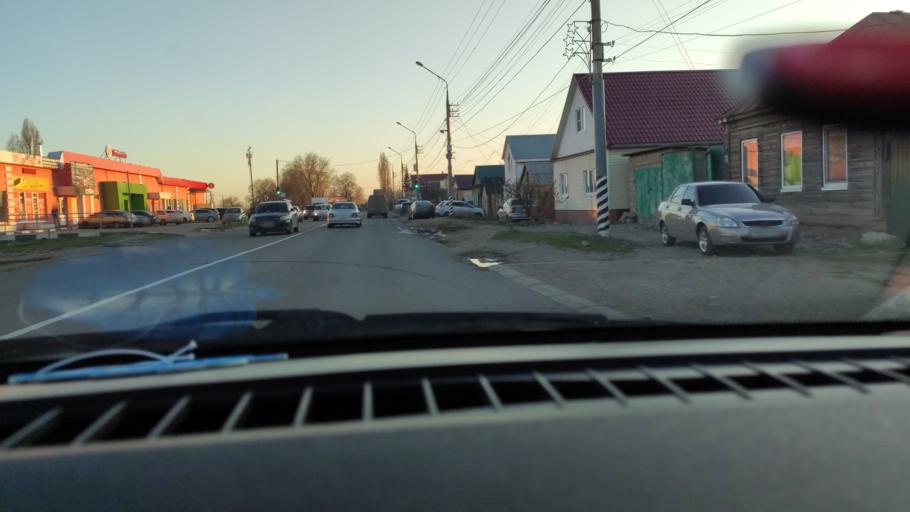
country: RU
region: Saratov
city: Privolzhskiy
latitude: 51.4242
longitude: 46.0464
